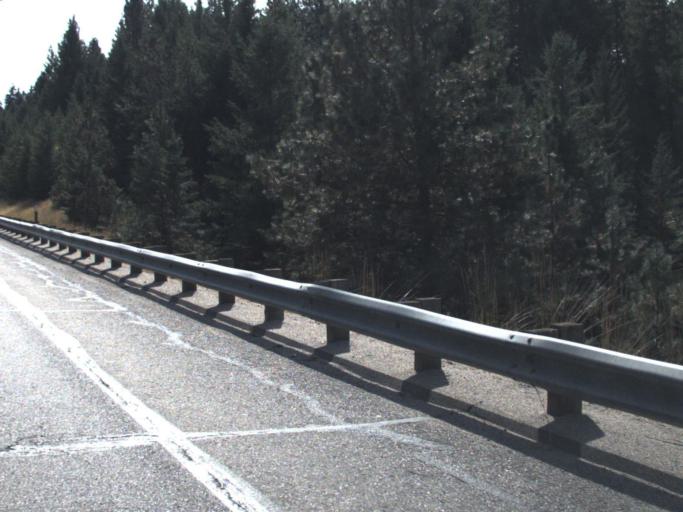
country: US
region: Washington
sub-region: Stevens County
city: Chewelah
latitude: 48.1309
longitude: -117.6539
